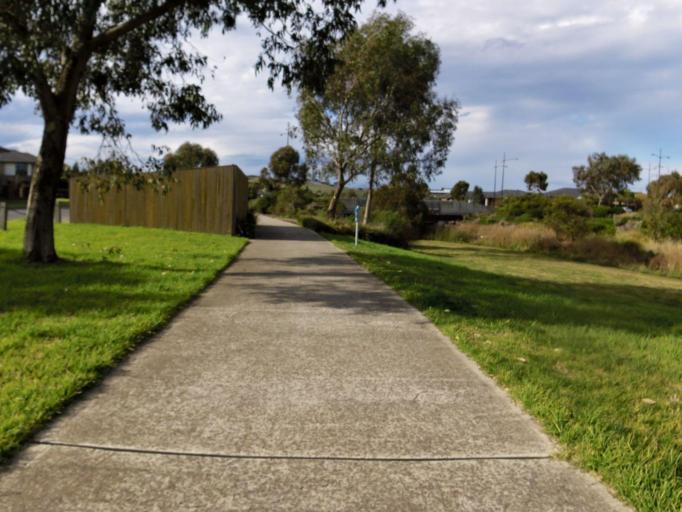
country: AU
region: Victoria
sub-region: Whittlesea
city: Epping
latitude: -37.6121
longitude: 145.0383
